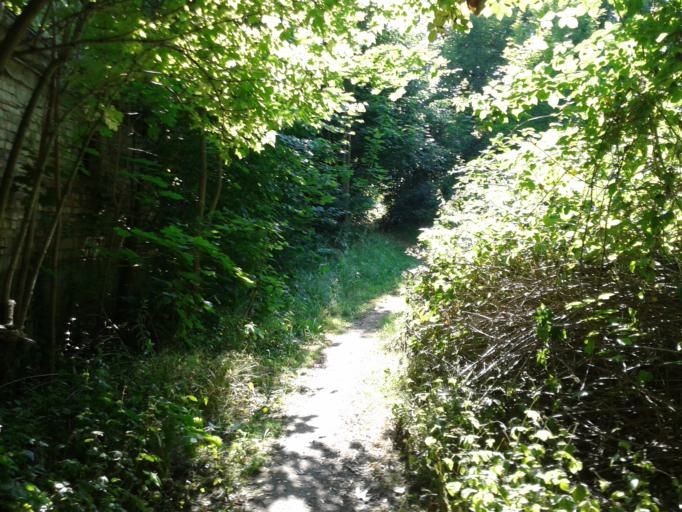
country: DE
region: Saxony
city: Bannewitz
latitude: 51.0047
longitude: 13.7301
